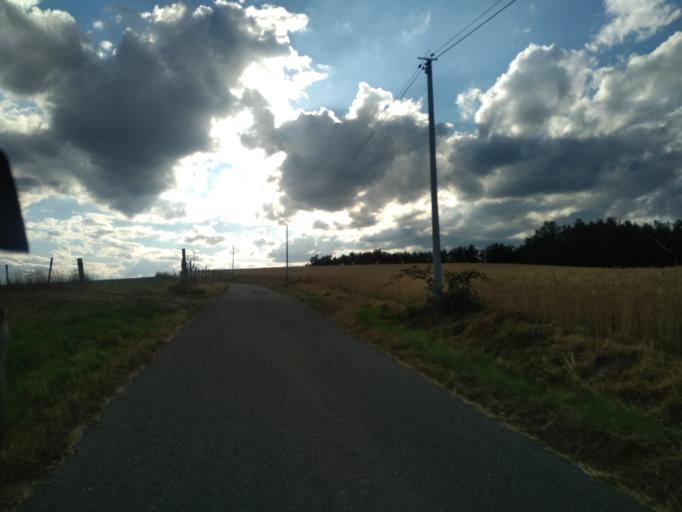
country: FR
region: Rhone-Alpes
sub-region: Departement de la Loire
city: Panissieres
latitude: 45.7434
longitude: 4.3333
